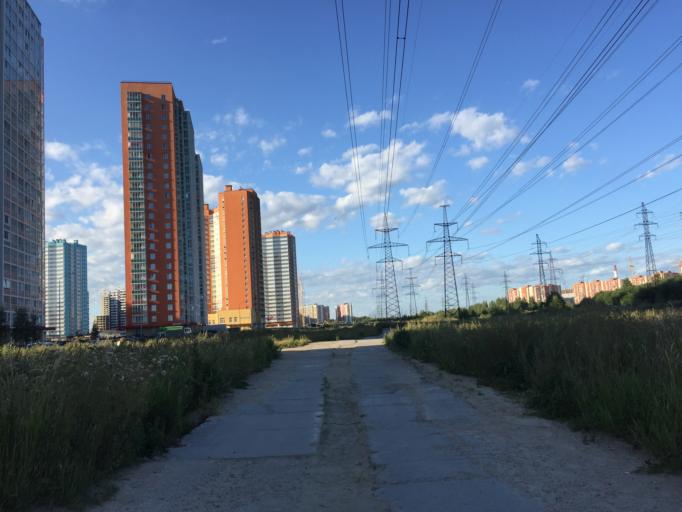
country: RU
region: Leningrad
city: Murino
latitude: 60.0567
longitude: 30.4430
